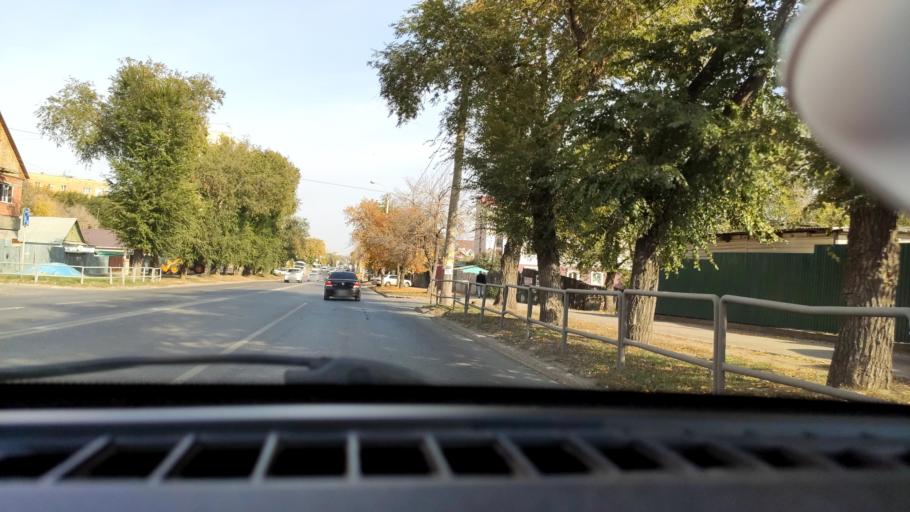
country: RU
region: Samara
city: Samara
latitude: 53.1854
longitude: 50.2033
